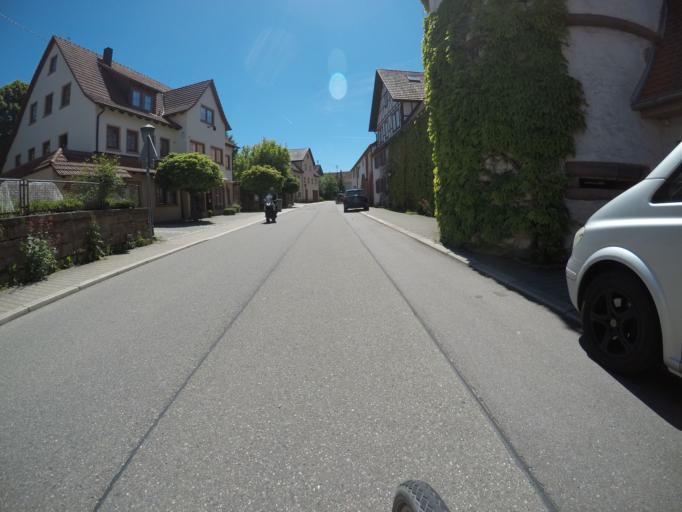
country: DE
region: Baden-Wuerttemberg
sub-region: Karlsruhe Region
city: Friolzheim
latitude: 48.8058
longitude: 8.8223
